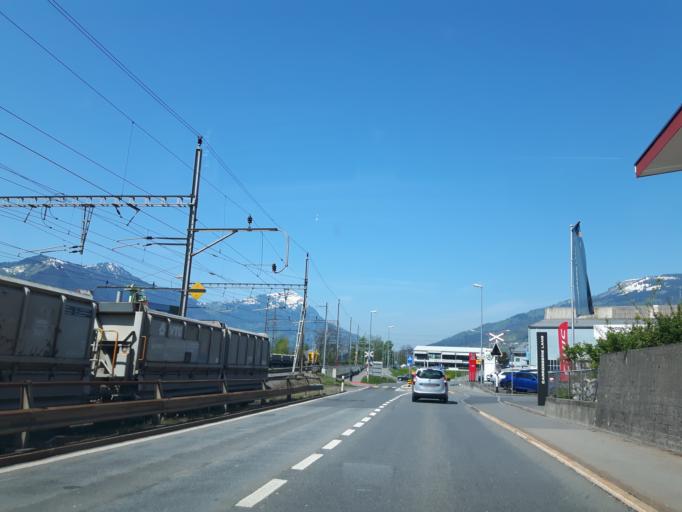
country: CH
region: Schwyz
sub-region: Bezirk Schwyz
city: Ibach
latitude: 47.0298
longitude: 8.6286
